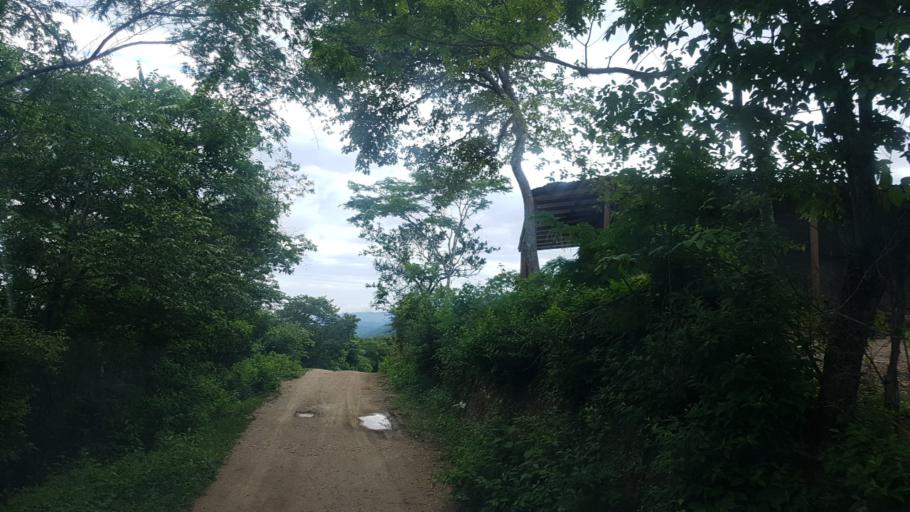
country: NI
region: Nueva Segovia
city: Mozonte
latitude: 13.5923
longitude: -86.4152
